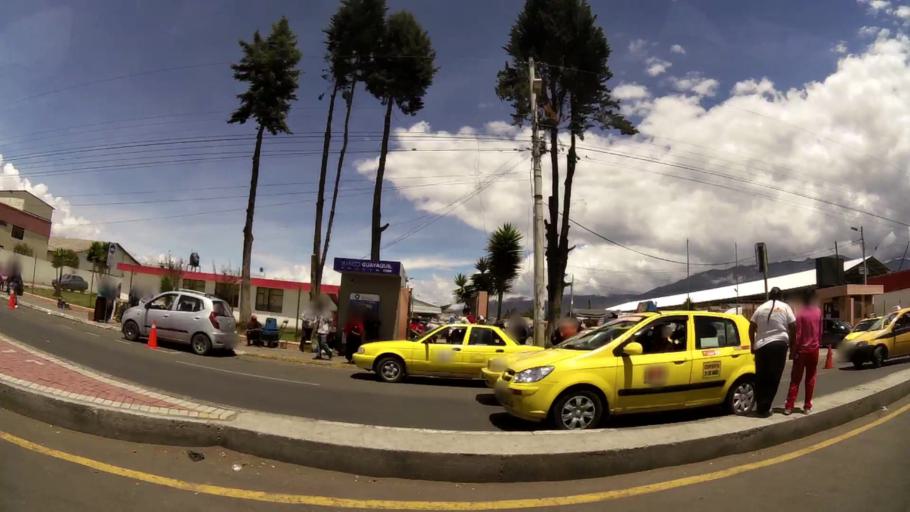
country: EC
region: Chimborazo
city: Riobamba
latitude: -1.6871
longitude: -78.6336
